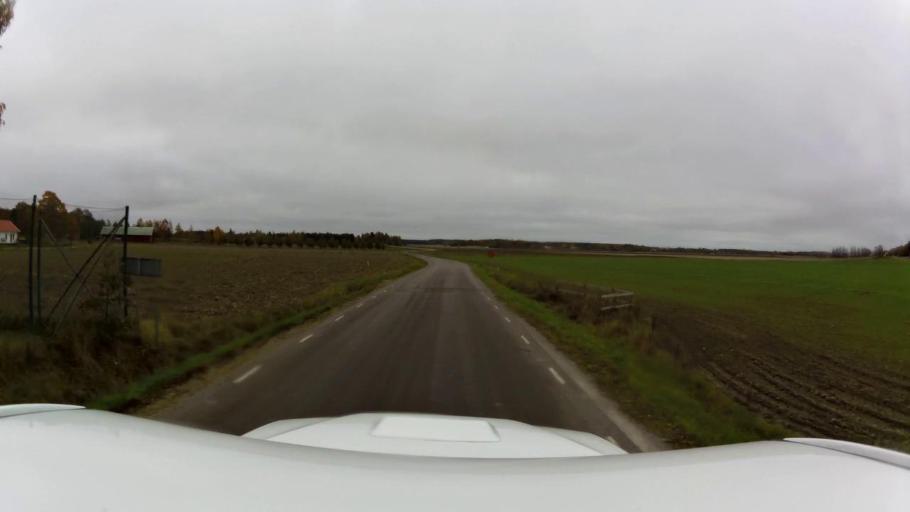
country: SE
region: OEstergoetland
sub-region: Linkopings Kommun
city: Linghem
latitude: 58.4490
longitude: 15.7111
